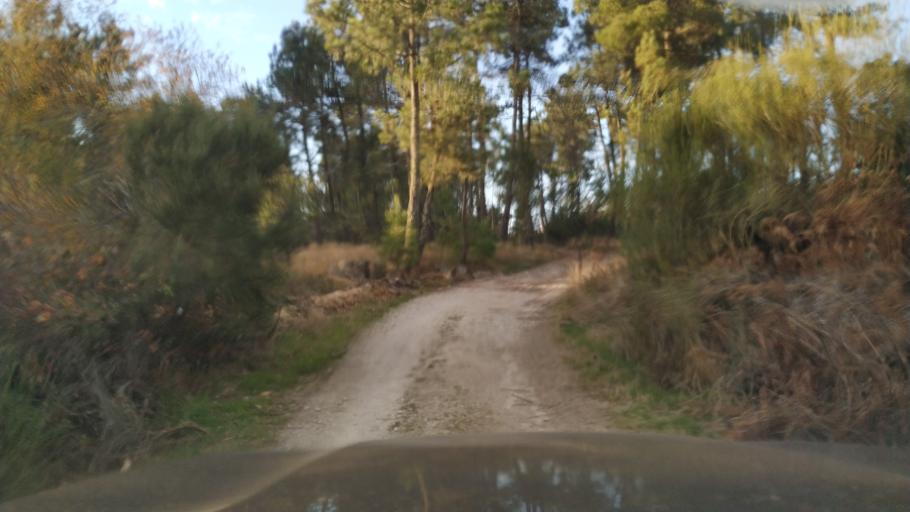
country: PT
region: Vila Real
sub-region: Sabrosa
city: Sabrosa
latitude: 41.3246
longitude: -7.6239
